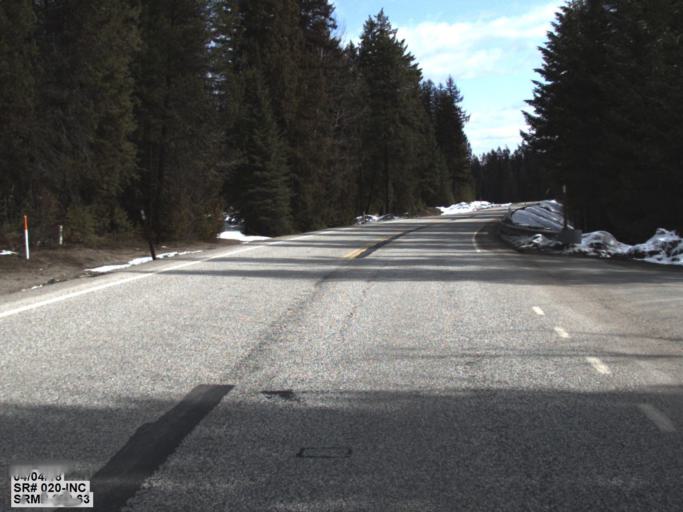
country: US
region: Washington
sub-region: Stevens County
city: Colville
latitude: 48.6320
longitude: -117.5413
